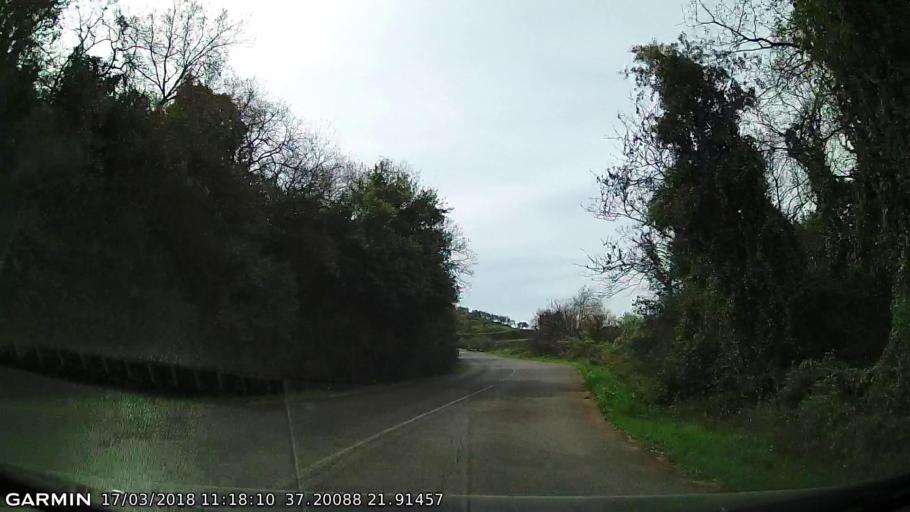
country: GR
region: Peloponnese
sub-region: Nomos Messinias
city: Meligalas
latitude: 37.2006
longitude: 21.9145
